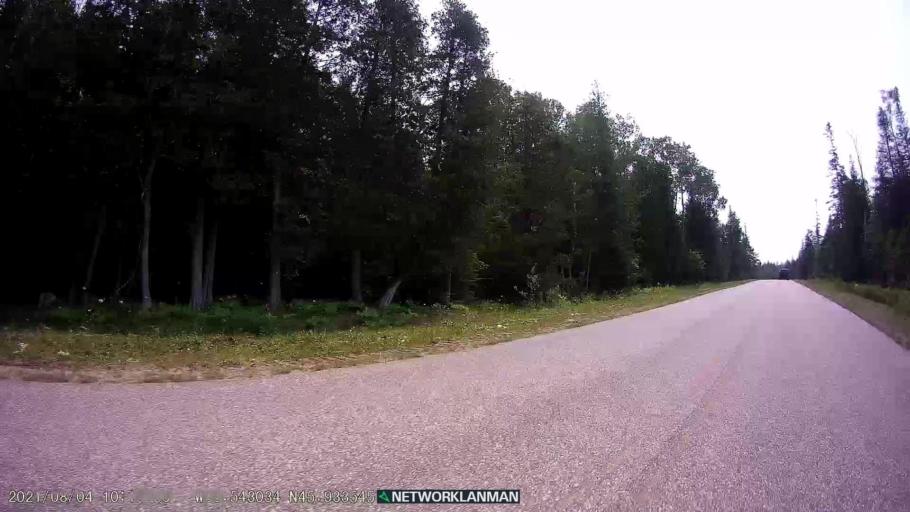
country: CA
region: Ontario
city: Thessalon
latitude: 45.9334
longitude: -83.5432
